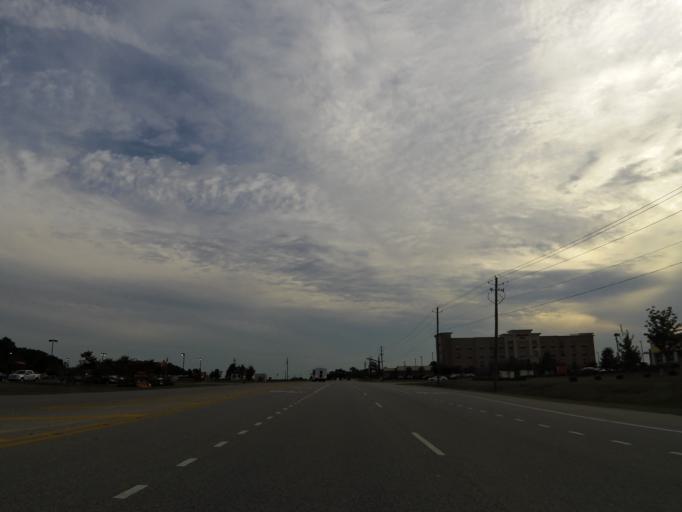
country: US
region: Alabama
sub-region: Escambia County
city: Atmore
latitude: 31.1072
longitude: -87.4763
